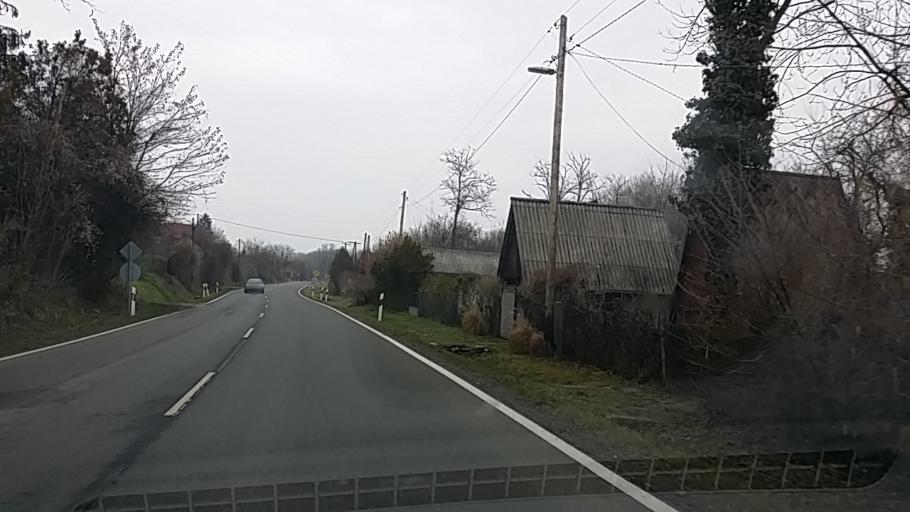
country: HU
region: Baranya
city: Mohacs
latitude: 46.0383
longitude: 18.7028
